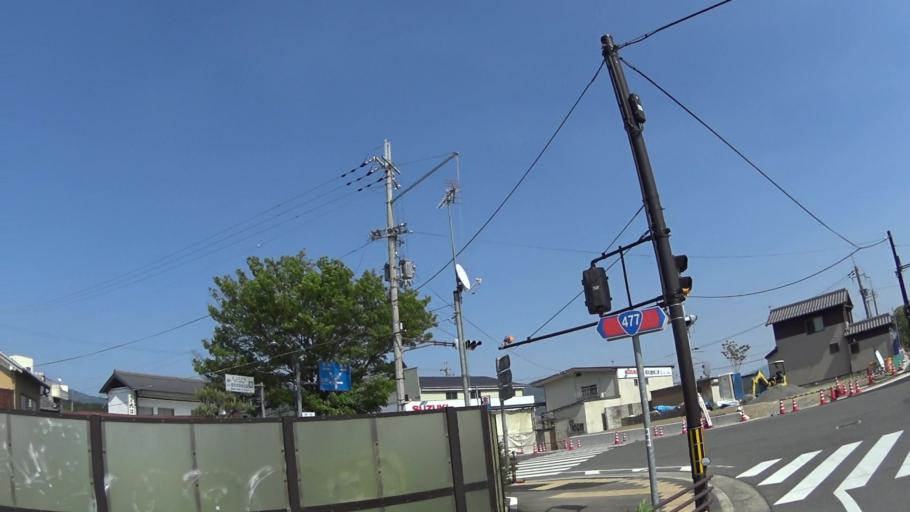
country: JP
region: Kyoto
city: Kameoka
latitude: 35.0723
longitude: 135.5380
